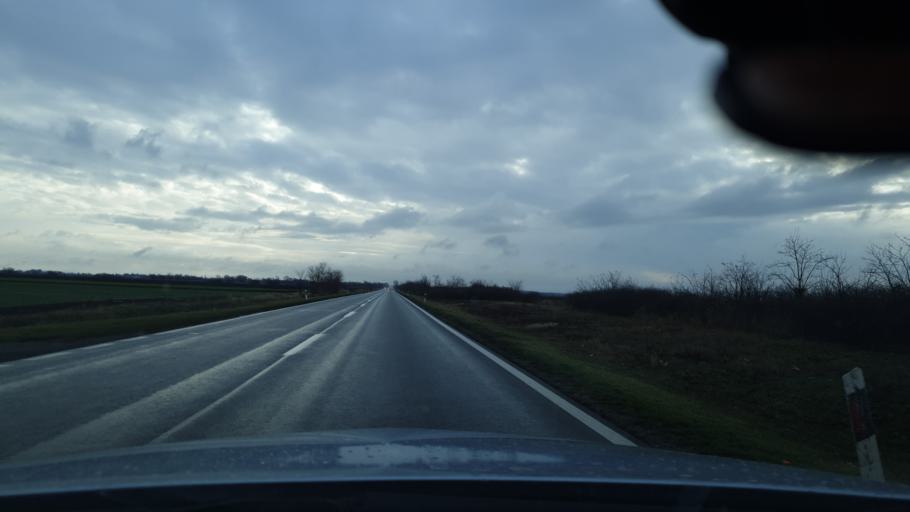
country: RS
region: Autonomna Pokrajina Vojvodina
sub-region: Juznobanatski Okrug
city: Kovin
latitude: 44.7770
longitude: 20.9358
